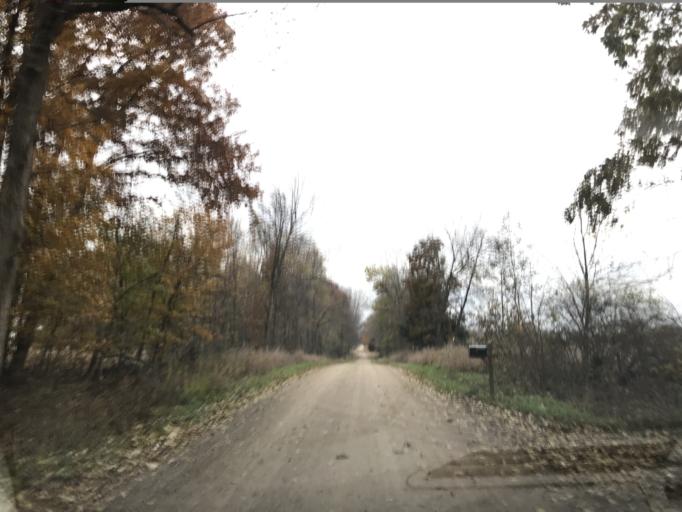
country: US
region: Michigan
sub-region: Lenawee County
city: Manitou Beach-Devils Lake
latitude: 42.0101
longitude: -84.3350
